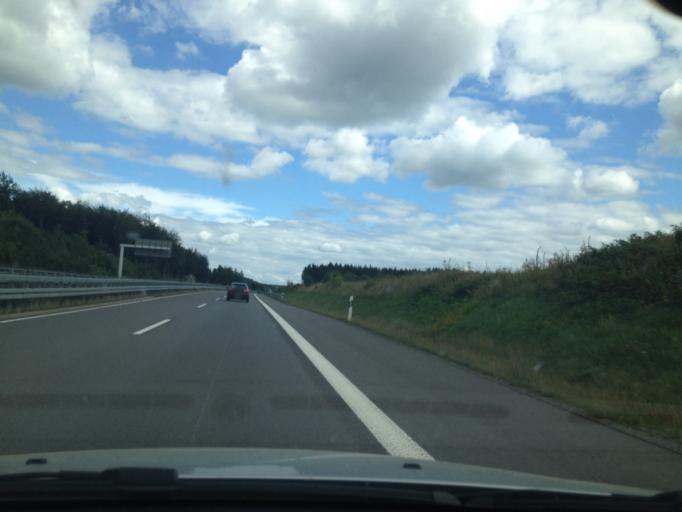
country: DE
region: North Rhine-Westphalia
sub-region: Regierungsbezirk Arnsberg
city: Wenden
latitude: 50.9948
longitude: 7.8792
